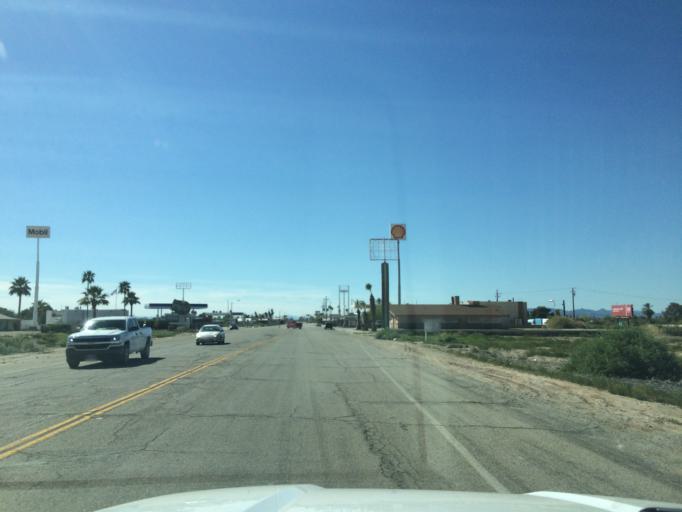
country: US
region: California
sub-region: Riverside County
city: Blythe
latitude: 33.6108
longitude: -114.5686
